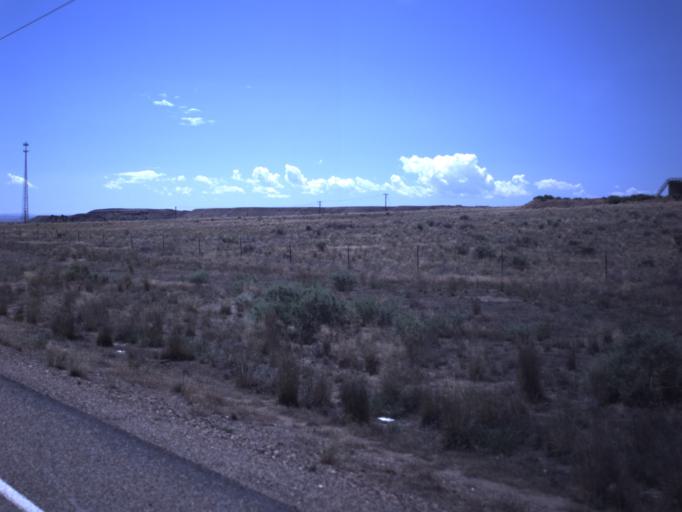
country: US
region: Utah
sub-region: Uintah County
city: Naples
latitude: 40.1289
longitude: -109.6639
